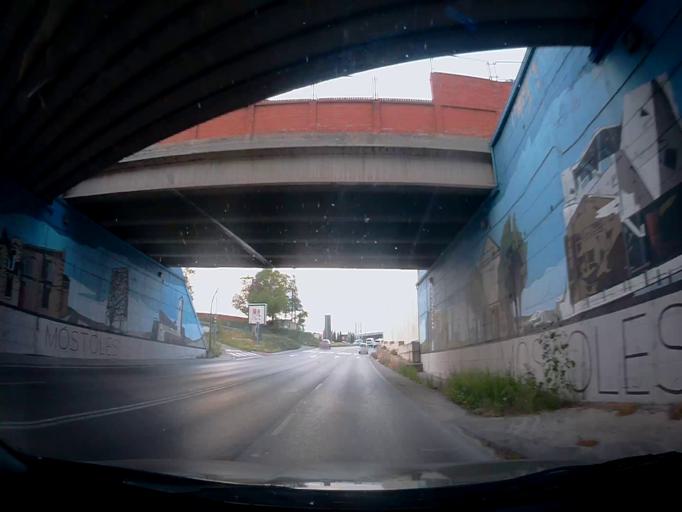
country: ES
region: Madrid
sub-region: Provincia de Madrid
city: Mostoles
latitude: 40.3306
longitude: -3.8831
